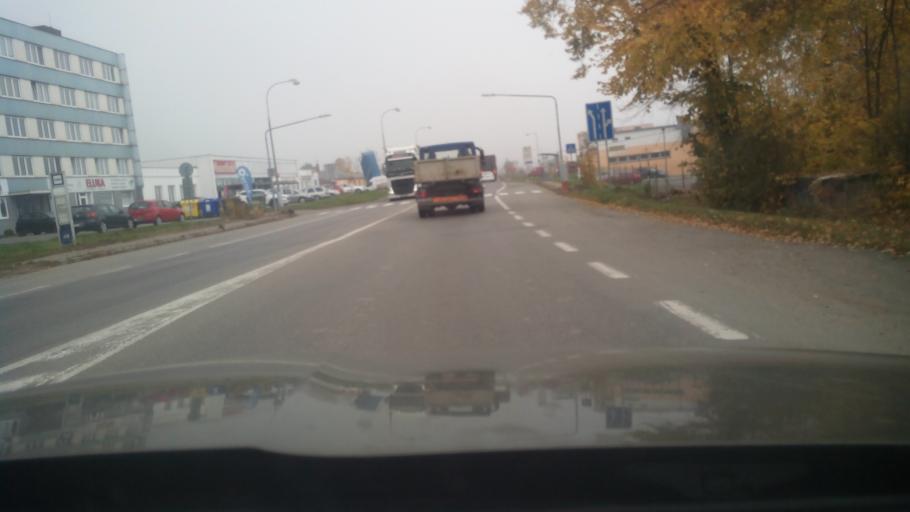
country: CZ
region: Jihocesky
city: Strakonice
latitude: 49.2685
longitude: 13.9165
